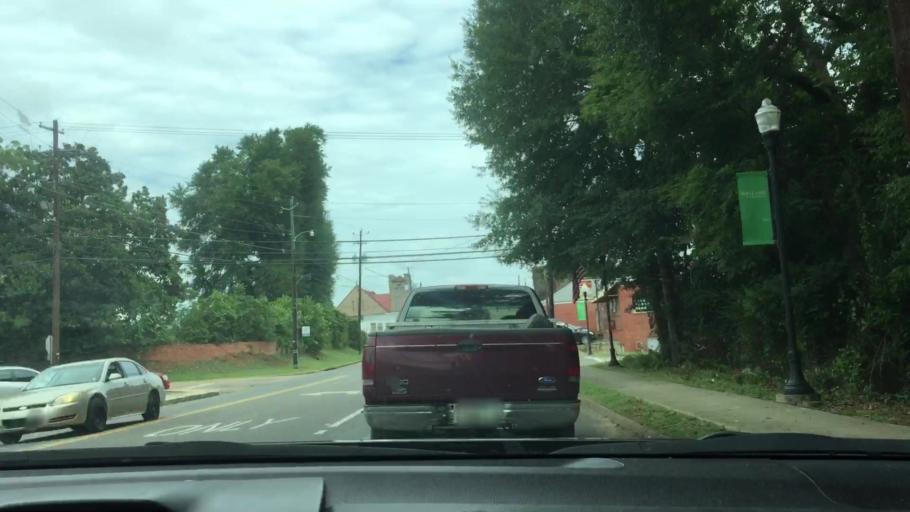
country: US
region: Alabama
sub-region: Hale County
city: Greensboro
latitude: 32.7025
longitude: -87.5954
